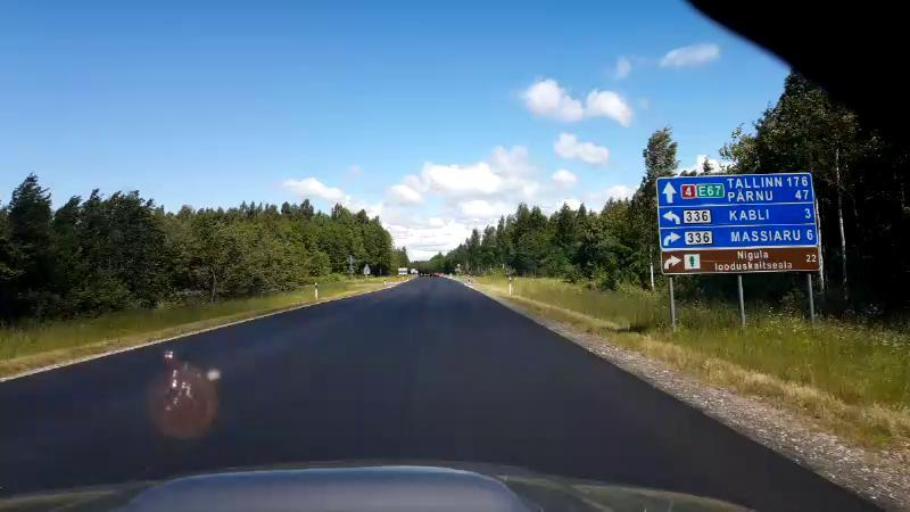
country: LV
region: Salacgrivas
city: Ainazi
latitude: 58.0119
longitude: 24.4920
